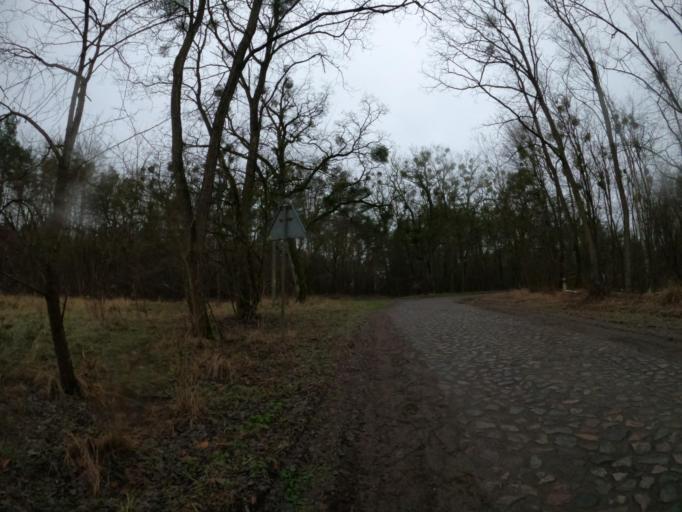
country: PL
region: West Pomeranian Voivodeship
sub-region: Powiat mysliborski
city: Debno
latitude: 52.8020
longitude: 14.7485
